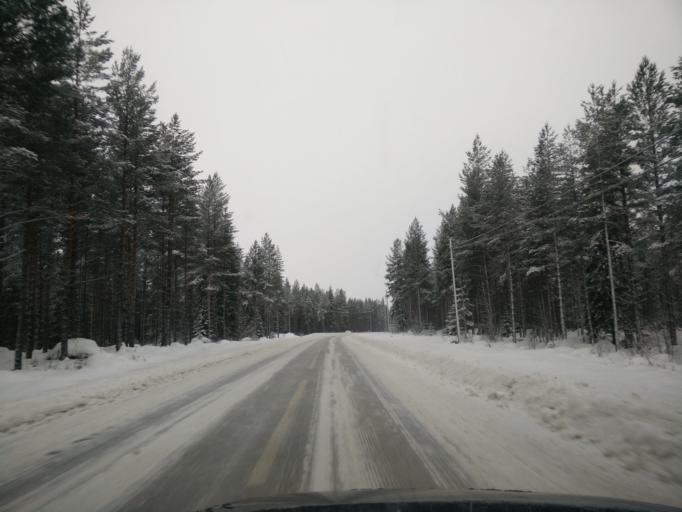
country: SE
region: Jaemtland
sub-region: Braecke Kommun
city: Braecke
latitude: 62.3968
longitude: 15.1839
